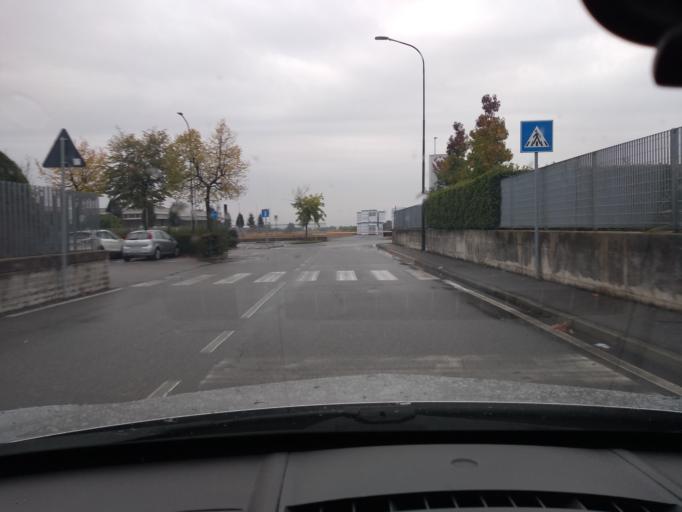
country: IT
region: Lombardy
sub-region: Provincia di Bergamo
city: Mornico al Serio
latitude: 45.5902
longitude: 9.7882
